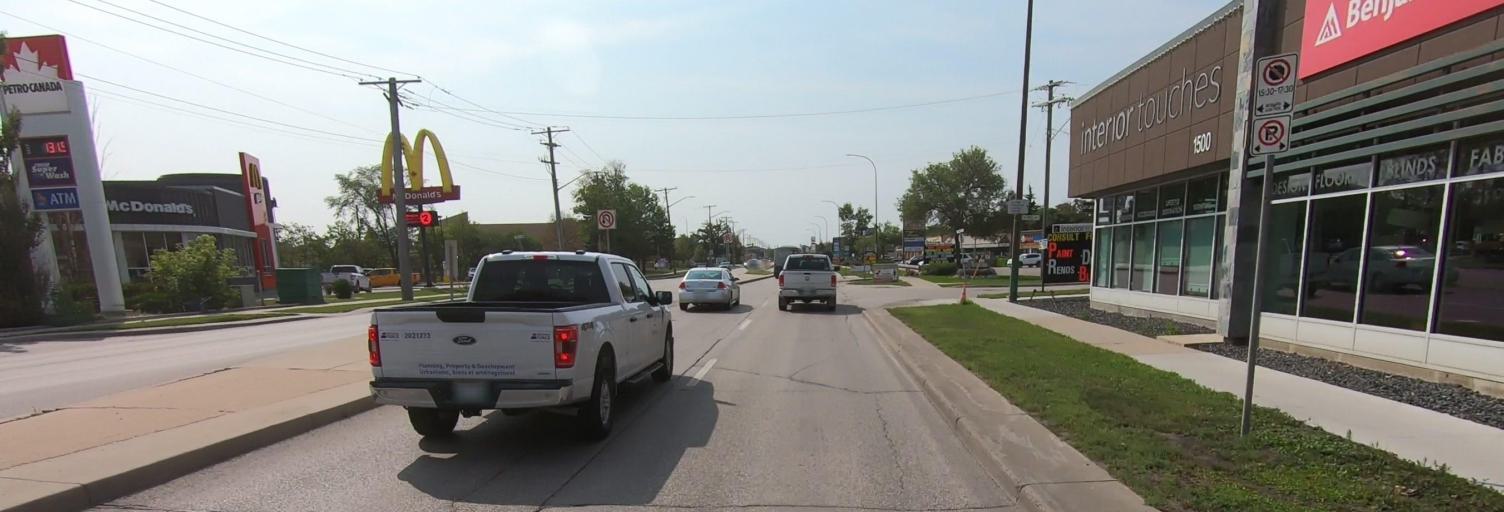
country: CA
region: Manitoba
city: Winnipeg
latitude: 49.8270
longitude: -97.1146
